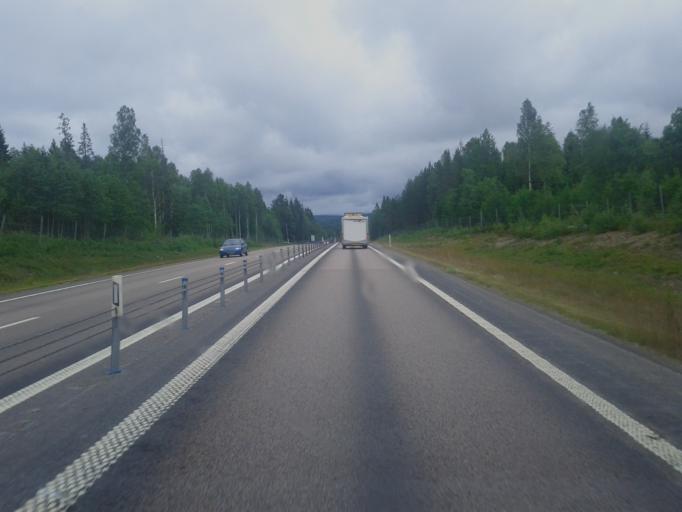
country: SE
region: Vaesternorrland
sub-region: Haernoesands Kommun
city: Haernoesand
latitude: 62.5696
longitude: 17.7399
